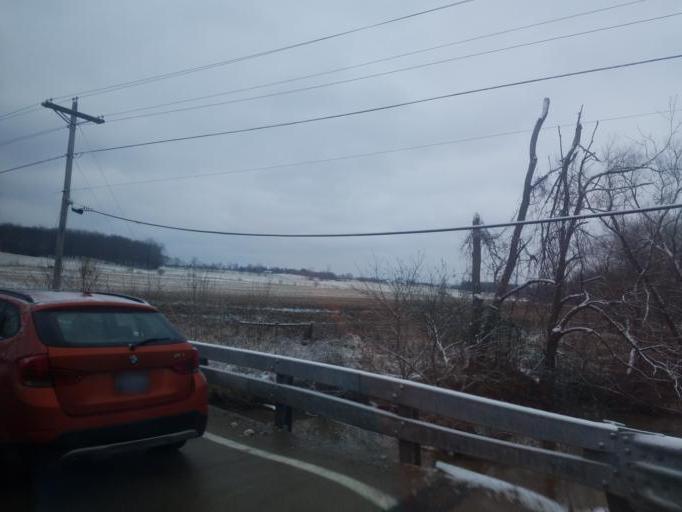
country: US
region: Ohio
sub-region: Licking County
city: Johnstown
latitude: 40.1416
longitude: -82.6924
